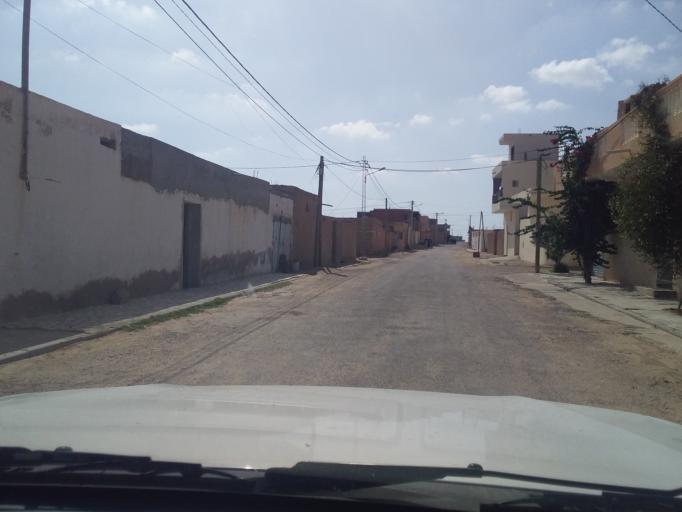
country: TN
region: Madanin
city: Medenine
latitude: 33.5824
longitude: 10.3237
